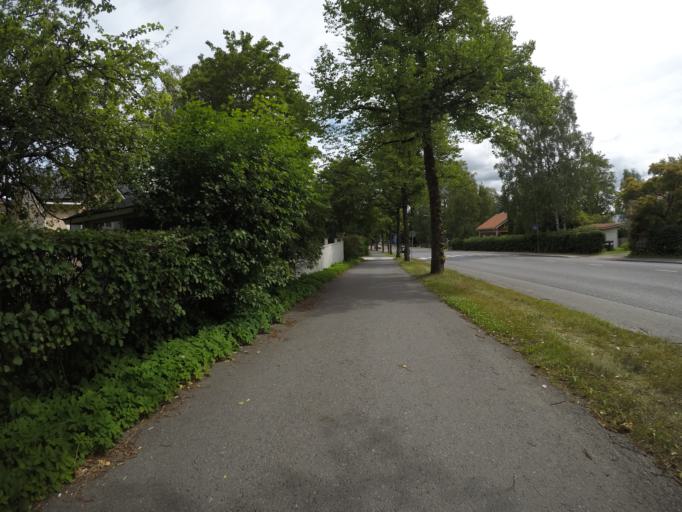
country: FI
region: Haeme
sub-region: Haemeenlinna
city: Haemeenlinna
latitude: 61.0034
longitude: 24.4921
